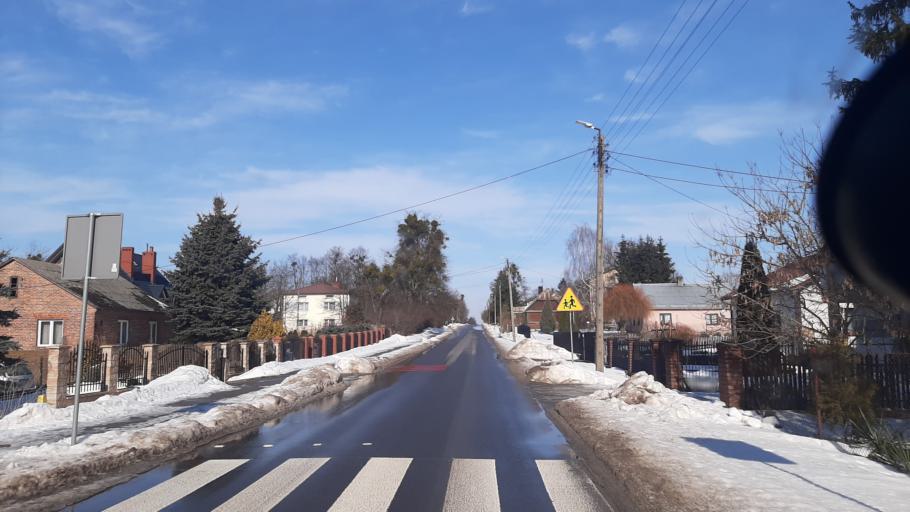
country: PL
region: Lublin Voivodeship
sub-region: Powiat pulawski
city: Wawolnica
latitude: 51.3327
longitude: 22.1094
